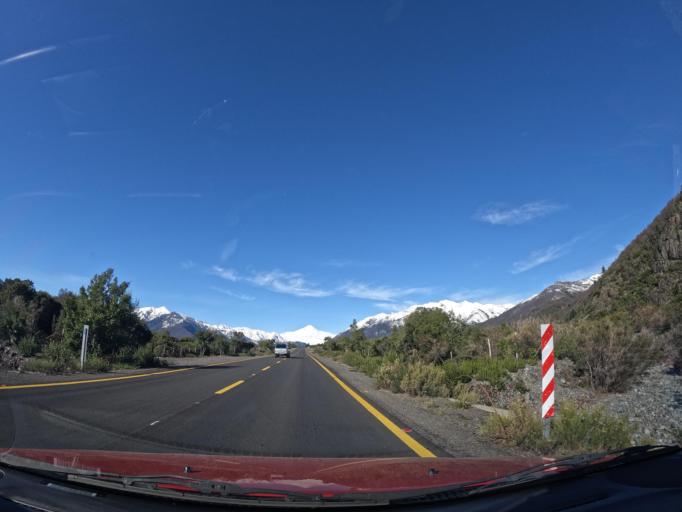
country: CL
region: Biobio
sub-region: Provincia de Biobio
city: Mulchen
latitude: -37.3401
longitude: -71.6014
